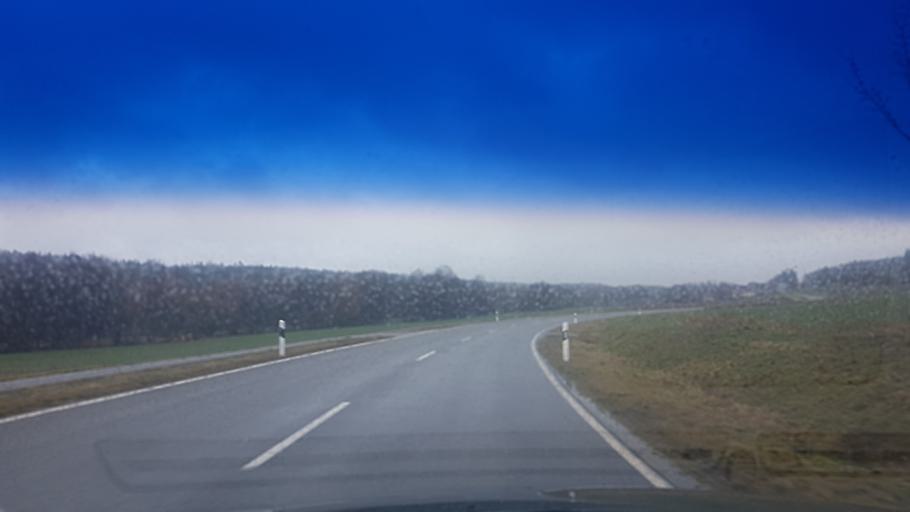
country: DE
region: Bavaria
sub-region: Upper Franconia
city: Pettstadt
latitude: 49.8455
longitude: 10.9042
